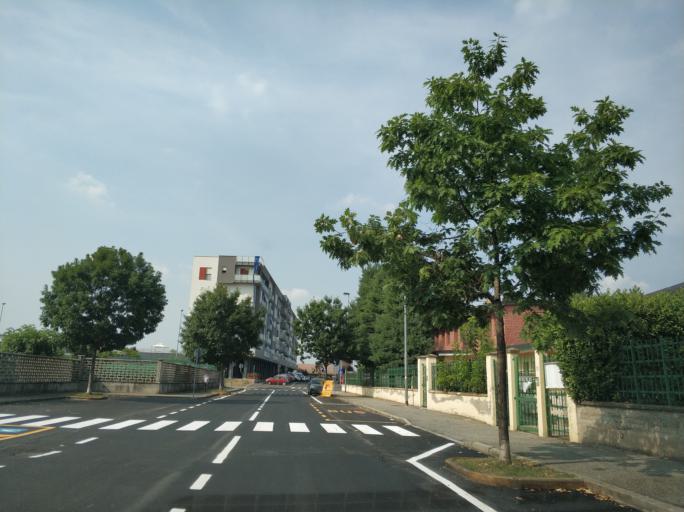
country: IT
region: Piedmont
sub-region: Provincia di Torino
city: Leini
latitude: 45.1503
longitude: 7.7040
